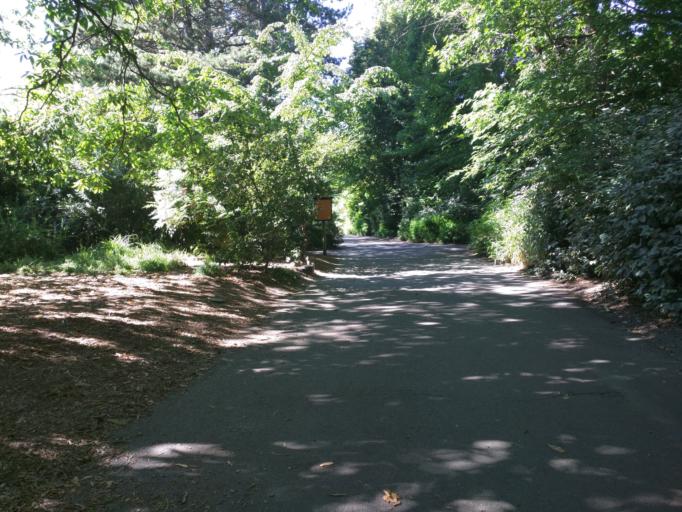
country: US
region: Washington
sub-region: King County
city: Seattle
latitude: 47.6684
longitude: -122.3492
